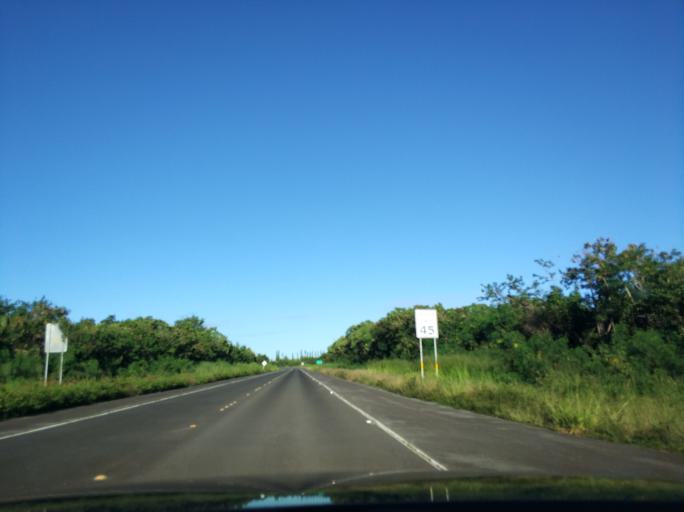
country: US
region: Hawaii
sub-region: Hawaii County
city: Leilani Estates
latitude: 19.3649
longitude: -154.9706
